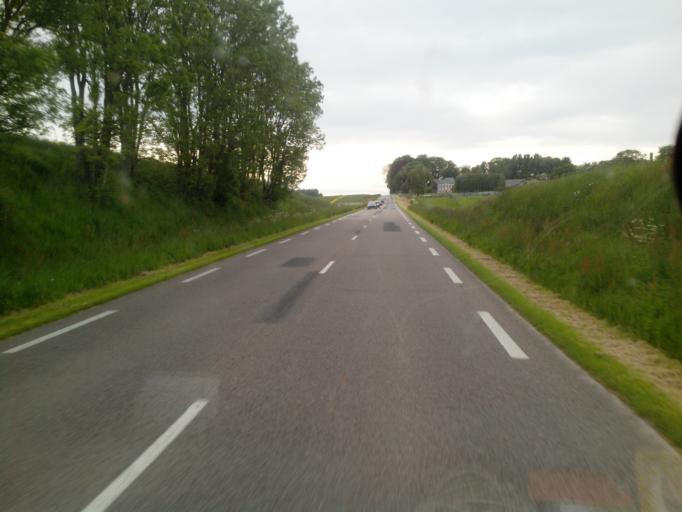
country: FR
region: Haute-Normandie
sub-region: Departement de la Seine-Maritime
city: Fauville-en-Caux
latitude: 49.6816
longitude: 0.5574
